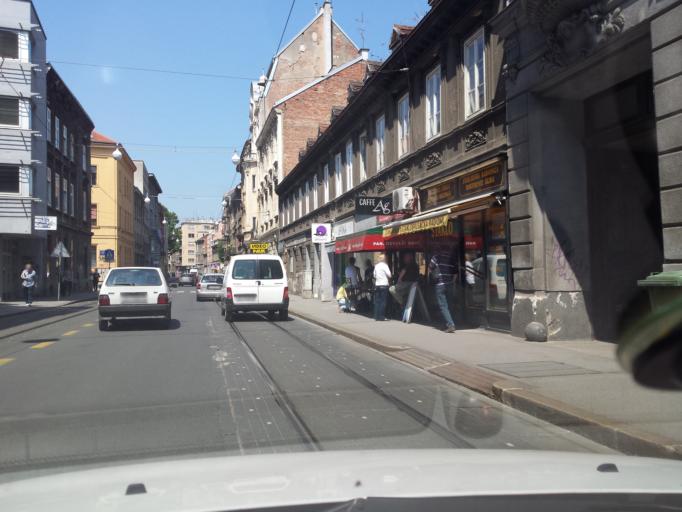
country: HR
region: Grad Zagreb
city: Zagreb - Centar
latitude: 45.8126
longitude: 15.9618
